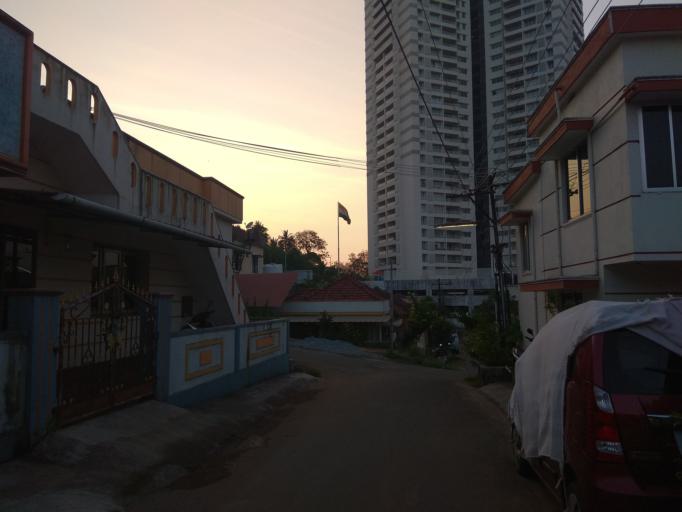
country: IN
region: Karnataka
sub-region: Dakshina Kannada
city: Mangalore
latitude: 12.8934
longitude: 74.8526
